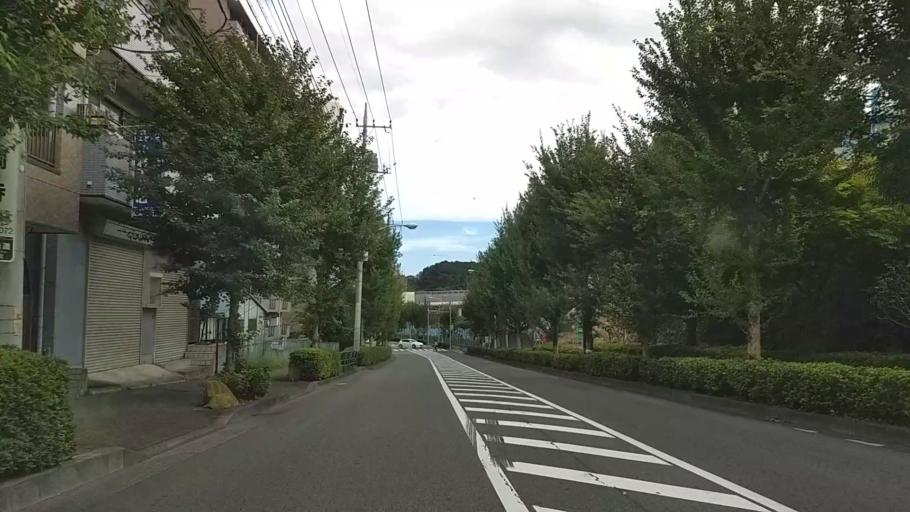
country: JP
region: Tokyo
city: Hachioji
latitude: 35.6441
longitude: 139.3506
